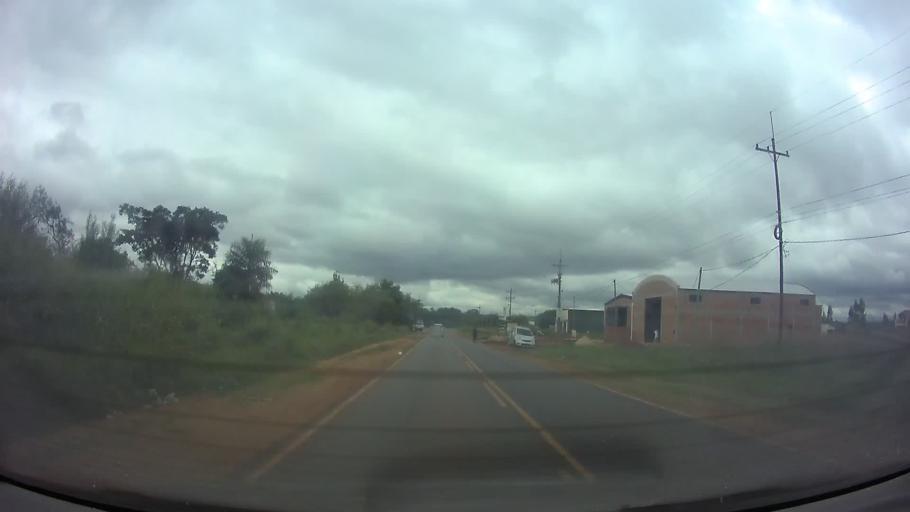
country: PY
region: Central
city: Guarambare
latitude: -25.4998
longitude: -57.4803
